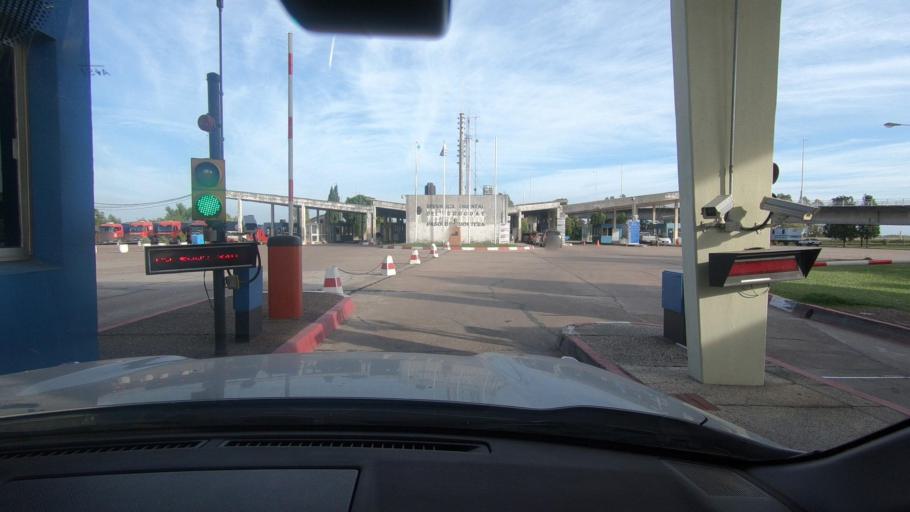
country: AR
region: Entre Rios
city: Colon
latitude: -32.2565
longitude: -58.1376
